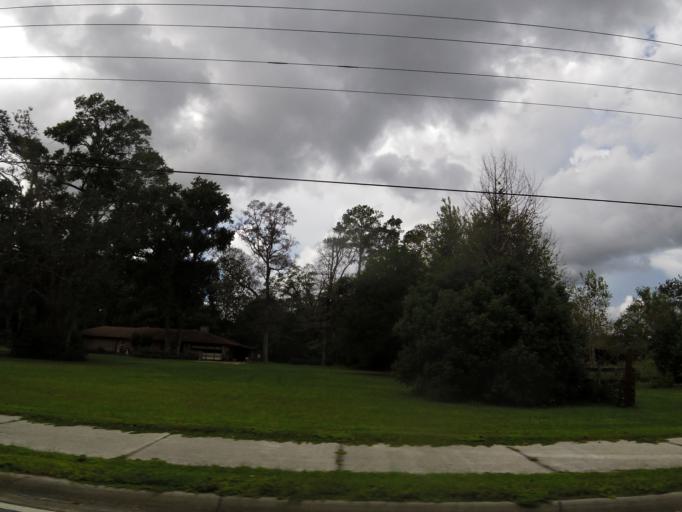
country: US
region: Florida
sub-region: Clay County
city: Asbury Lake
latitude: 30.0928
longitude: -81.8098
